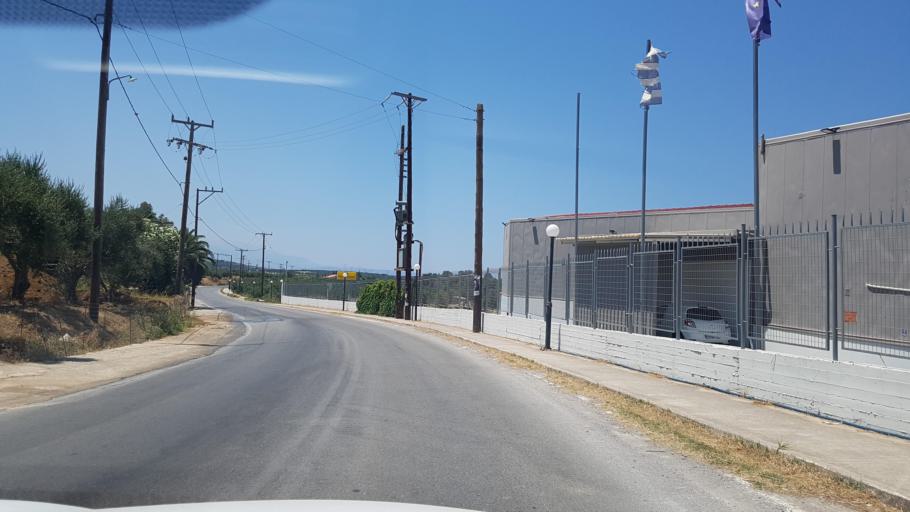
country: GR
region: Crete
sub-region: Nomos Rethymnis
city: Rethymno
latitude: 35.3575
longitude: 24.5807
